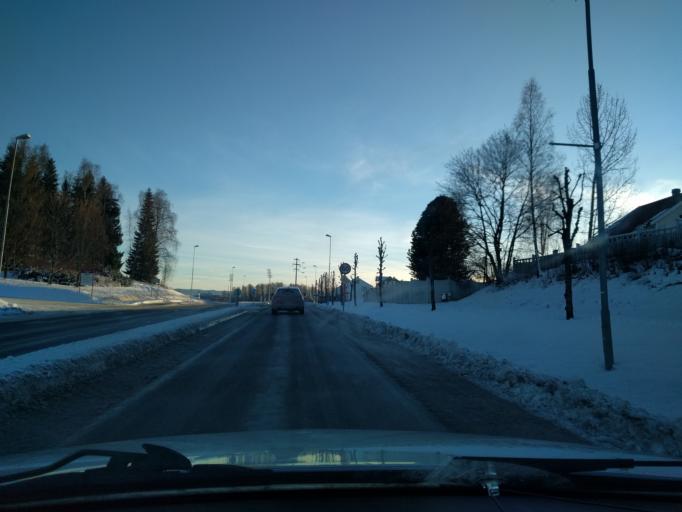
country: NO
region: Hedmark
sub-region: Hamar
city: Hamar
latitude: 60.8096
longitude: 11.0894
